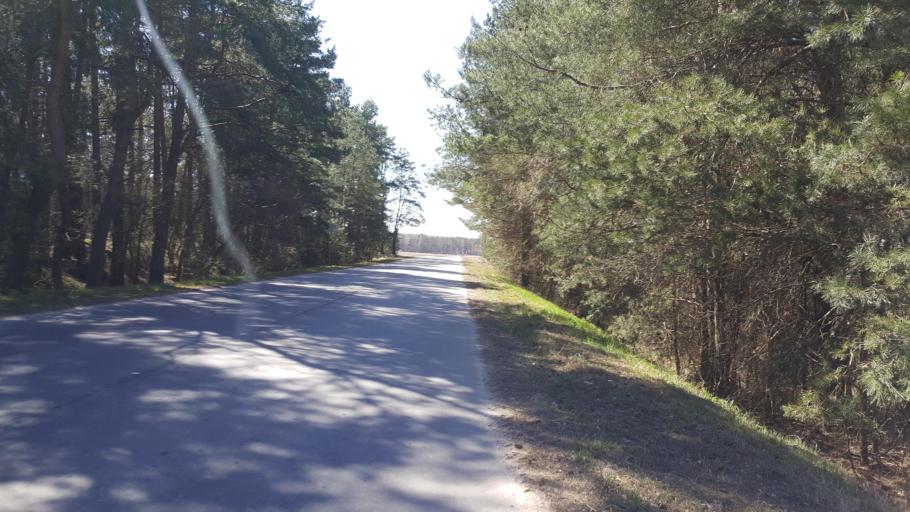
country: BY
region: Brest
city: Kamyanyets
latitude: 52.2850
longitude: 23.8529
